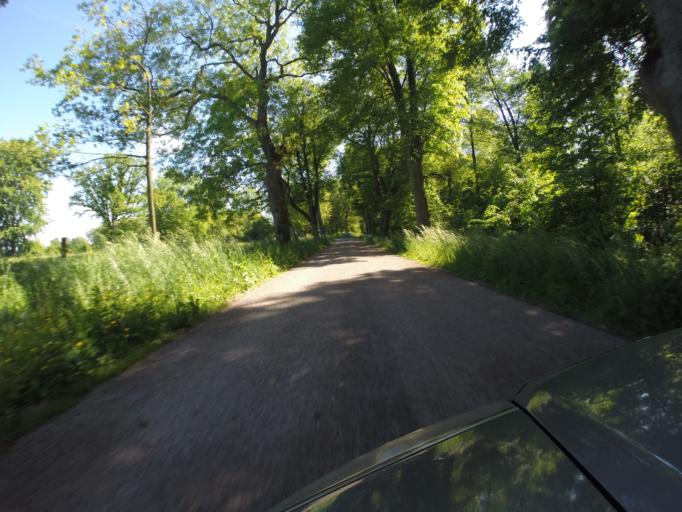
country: SE
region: Skane
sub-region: Helsingborg
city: Hyllinge
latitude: 56.0812
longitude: 12.8294
